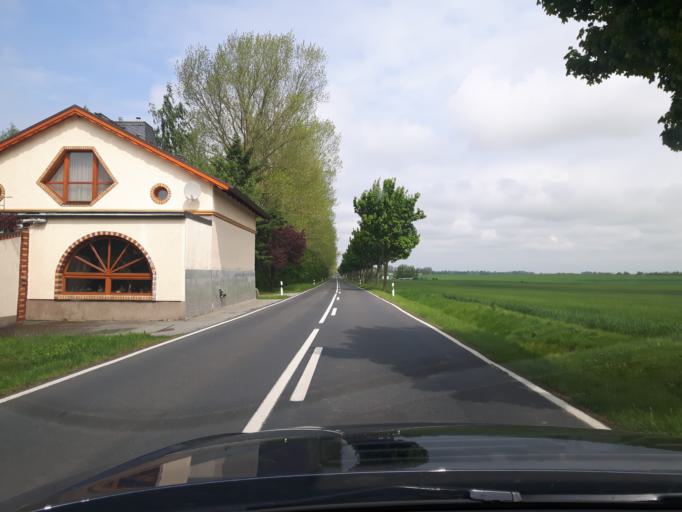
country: DE
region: Mecklenburg-Vorpommern
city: Barth
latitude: 54.2762
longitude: 12.7175
